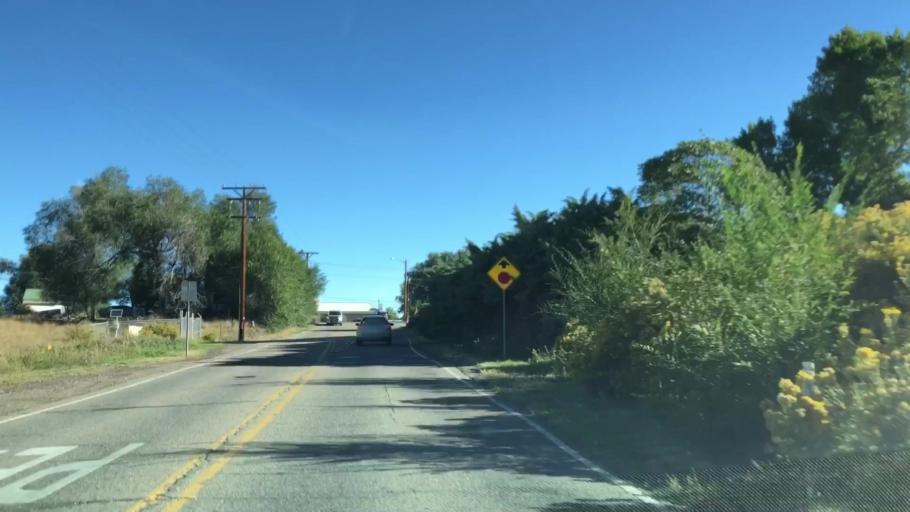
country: US
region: Colorado
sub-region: Larimer County
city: Loveland
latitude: 40.4060
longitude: -105.1214
